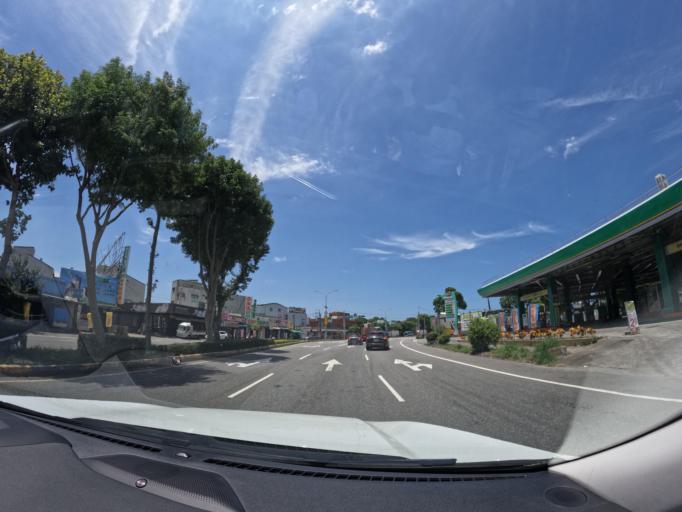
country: TW
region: Taiwan
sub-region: Taoyuan
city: Taoyuan
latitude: 25.0577
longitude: 121.3552
